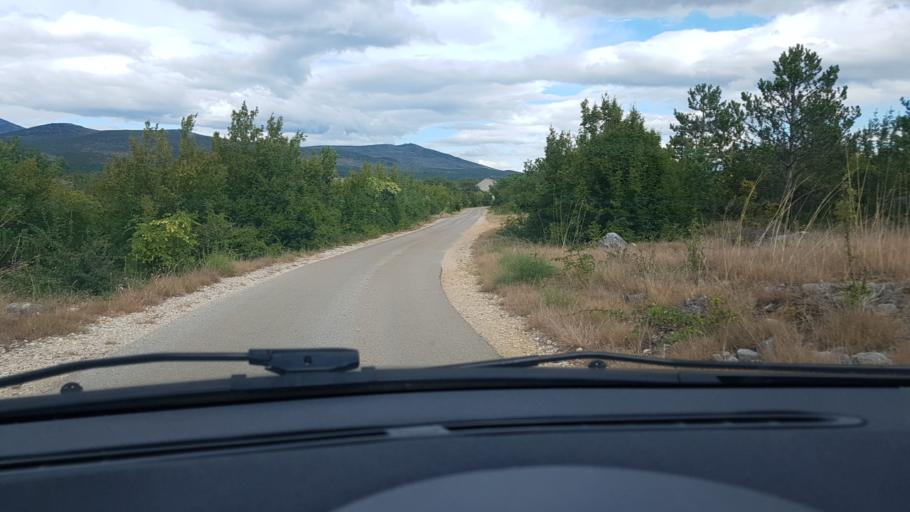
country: HR
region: Sibensko-Kniniska
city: Kistanje
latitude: 44.1109
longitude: 15.9224
